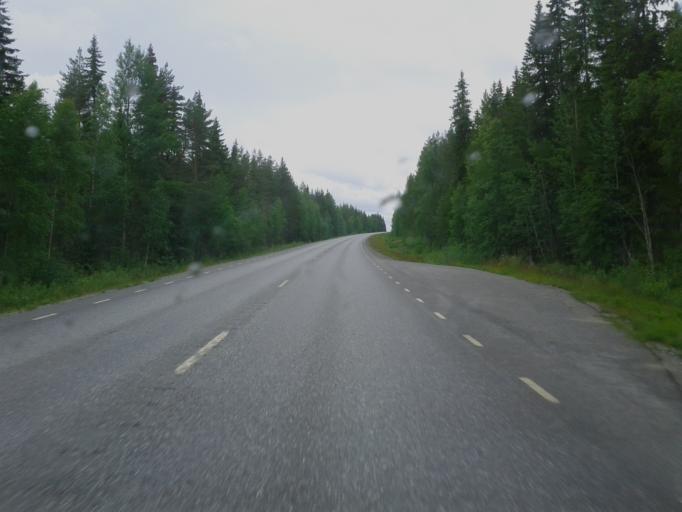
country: SE
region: Vaesterbotten
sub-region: Skelleftea Kommun
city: Langsele
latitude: 64.8966
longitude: 20.1531
